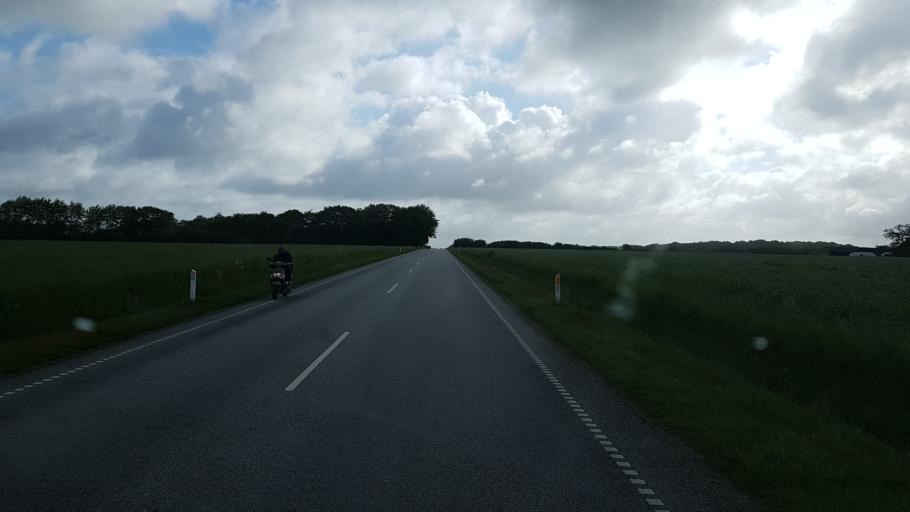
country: DK
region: South Denmark
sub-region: Vejen Kommune
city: Rodding
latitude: 55.3976
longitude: 9.1039
